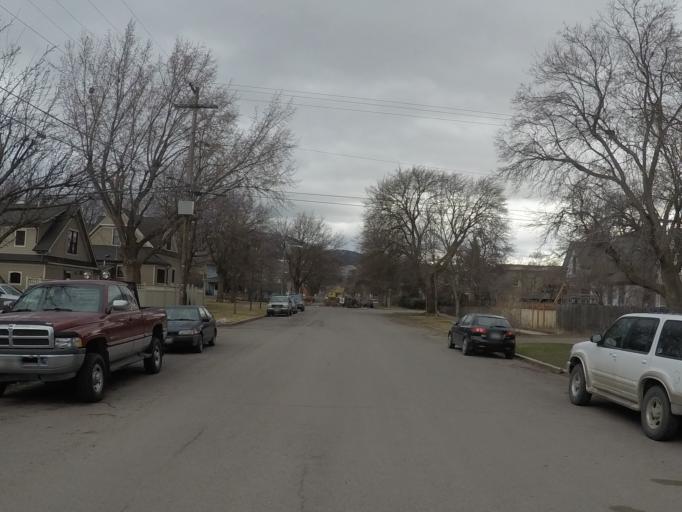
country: US
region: Montana
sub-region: Missoula County
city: Missoula
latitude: 46.8667
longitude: -114.0006
